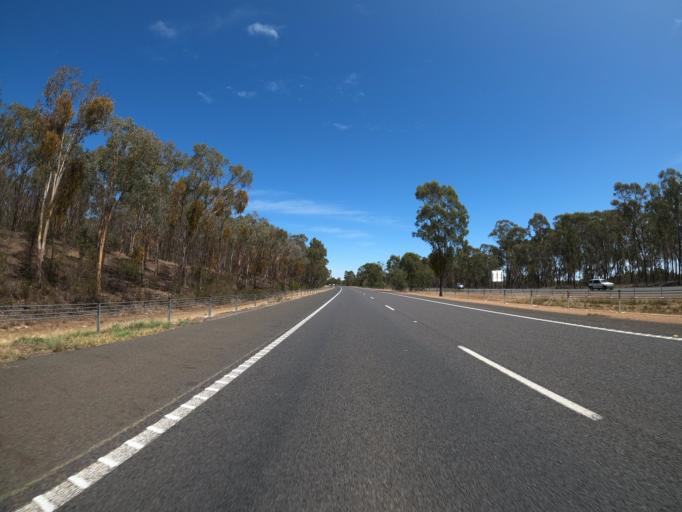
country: AU
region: Victoria
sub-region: Benalla
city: Benalla
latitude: -36.5776
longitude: 145.9391
